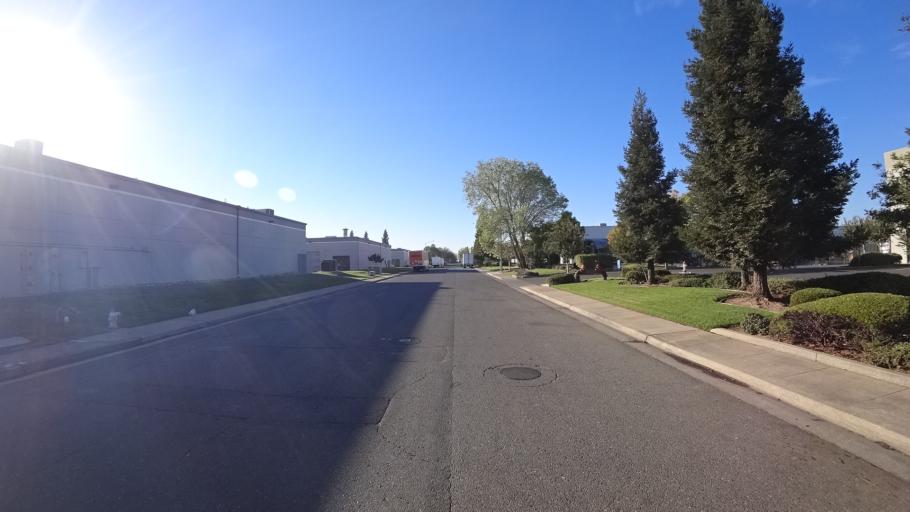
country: US
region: California
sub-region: Sacramento County
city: Florin
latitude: 38.5064
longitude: -121.3977
